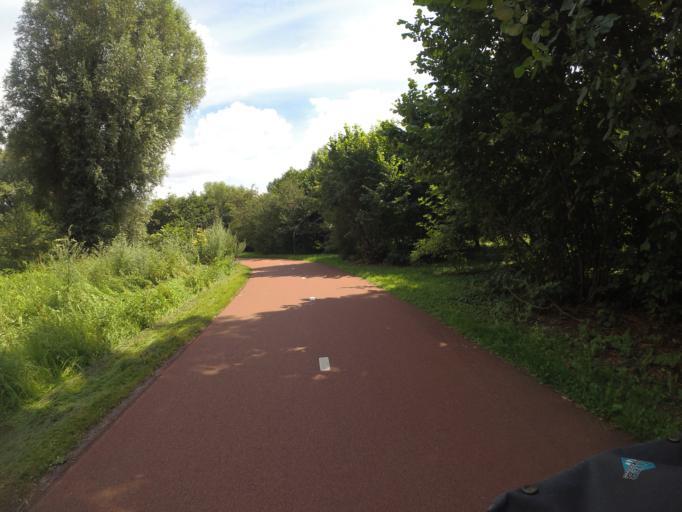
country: NL
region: North Brabant
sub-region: Gemeente Geldrop-Mierlo
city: Geldrop
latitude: 51.4292
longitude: 5.5534
